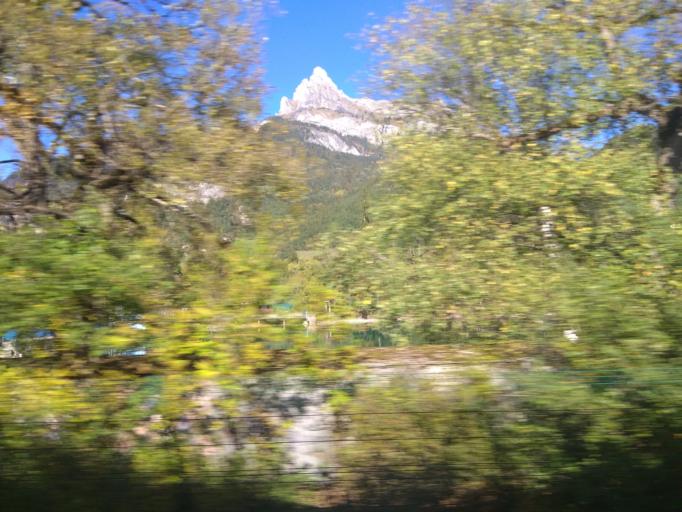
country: FR
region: Rhone-Alpes
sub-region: Departement de la Haute-Savoie
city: Domancy
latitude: 45.9233
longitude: 6.6547
